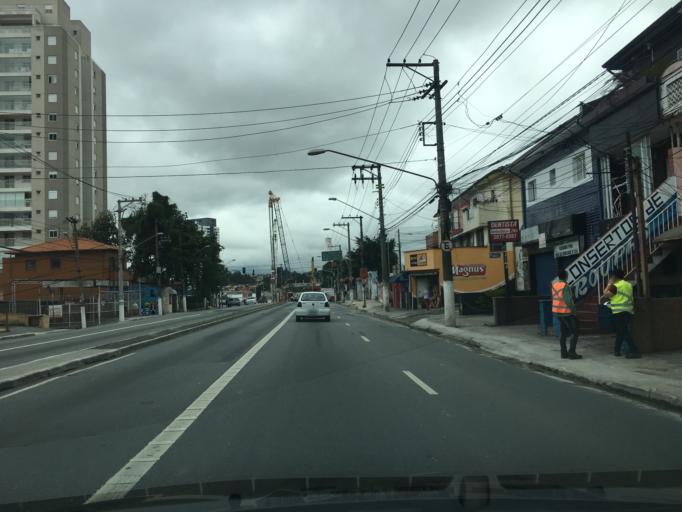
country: BR
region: Sao Paulo
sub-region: Taboao Da Serra
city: Taboao da Serra
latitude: -23.5976
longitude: -46.7404
